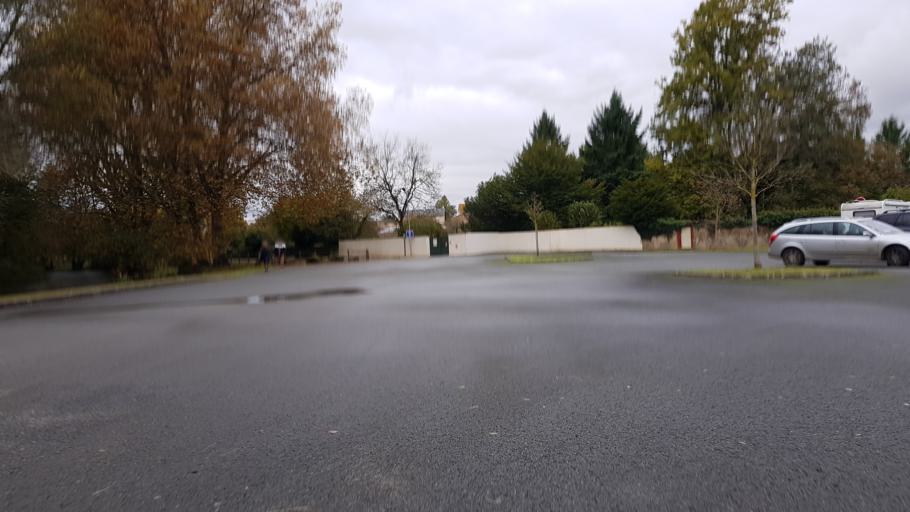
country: FR
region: Poitou-Charentes
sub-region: Departement de la Vienne
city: Chasseneuil-du-Poitou
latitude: 46.6373
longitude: 0.3610
